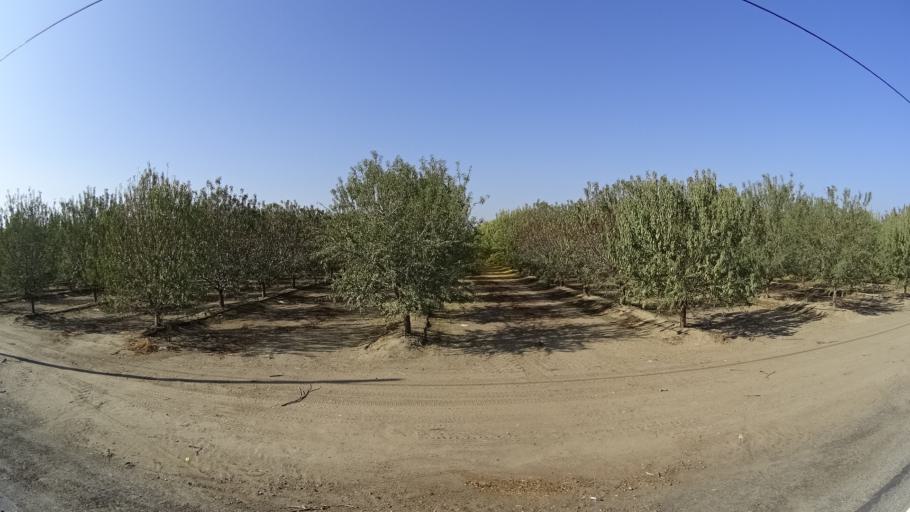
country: US
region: California
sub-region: Kern County
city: Greenfield
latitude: 35.2569
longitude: -119.0390
